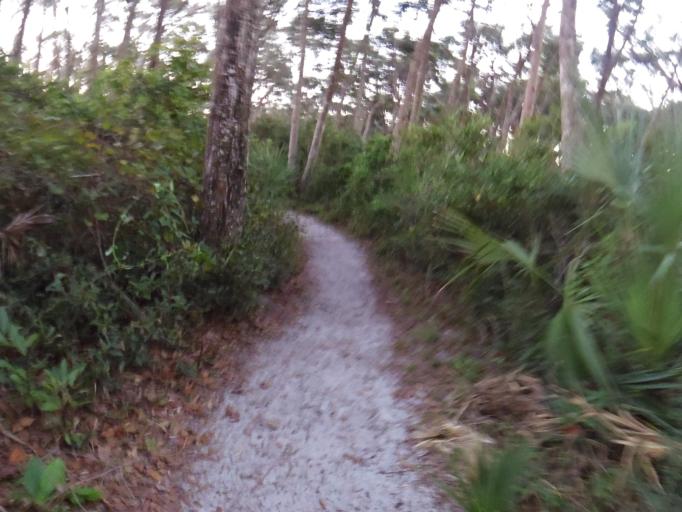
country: US
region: Florida
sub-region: Nassau County
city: Fernandina Beach
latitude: 30.5060
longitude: -81.4537
